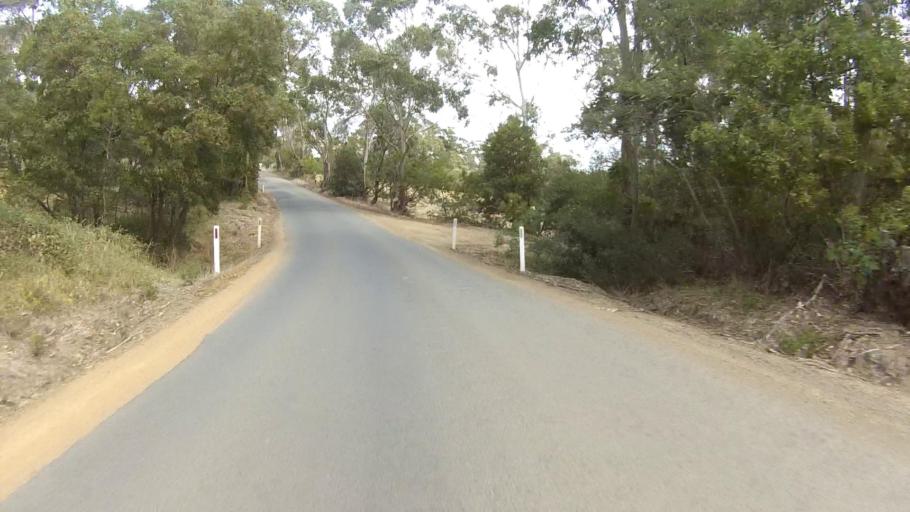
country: AU
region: Tasmania
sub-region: Kingborough
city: Blackmans Bay
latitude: -43.0341
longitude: 147.3067
